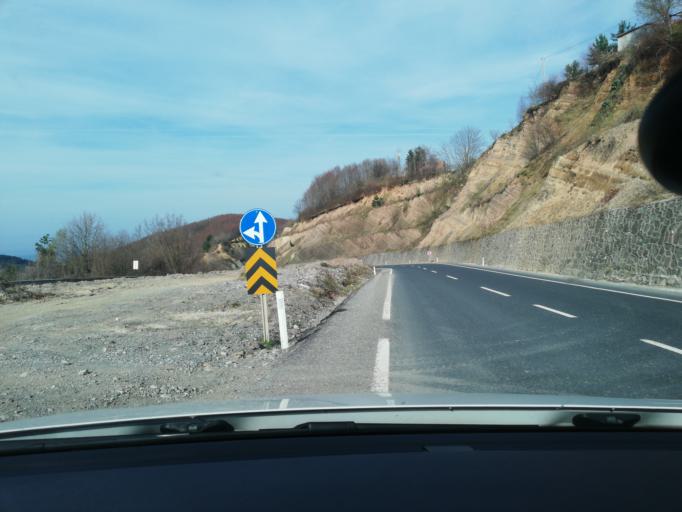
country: TR
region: Zonguldak
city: Kozlu
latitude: 41.3487
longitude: 31.6354
